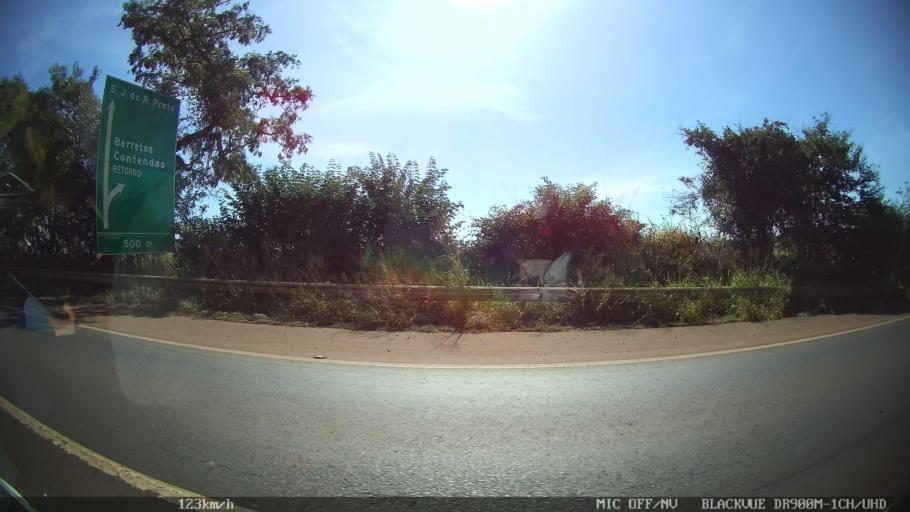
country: BR
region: Sao Paulo
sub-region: Barretos
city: Barretos
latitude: -20.5353
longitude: -48.6052
